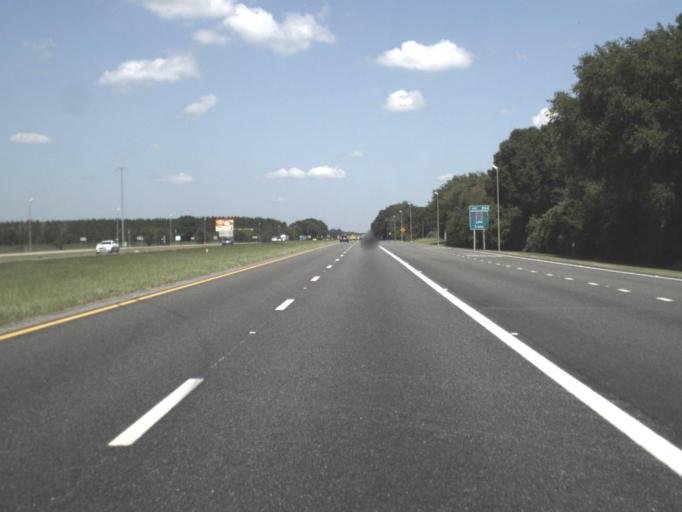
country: US
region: Florida
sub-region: Madison County
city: Madison
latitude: 30.3751
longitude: -83.2763
